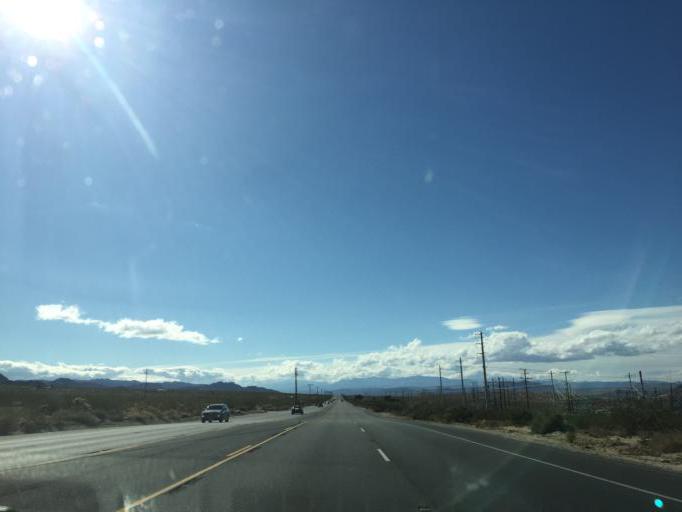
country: US
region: California
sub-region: San Bernardino County
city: Twentynine Palms
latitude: 34.1352
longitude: -116.1771
